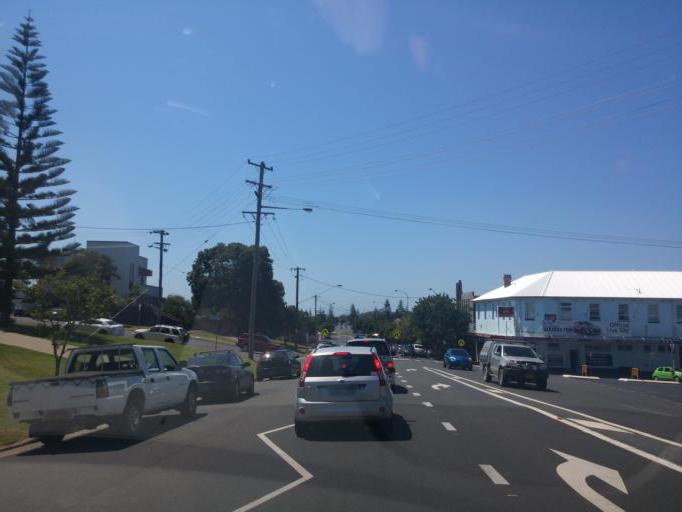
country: AU
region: New South Wales
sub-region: Coffs Harbour
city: Coffs Harbour
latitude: -30.3045
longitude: 153.1356
